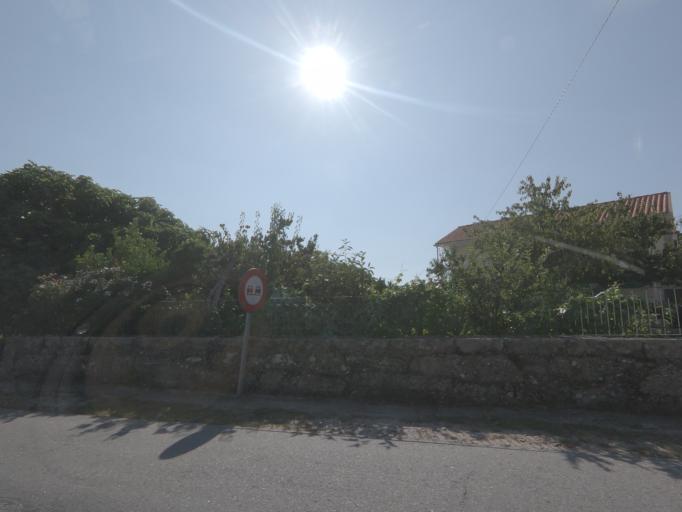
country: PT
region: Viseu
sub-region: Moimenta da Beira
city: Moimenta da Beira
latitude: 40.9907
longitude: -7.5620
